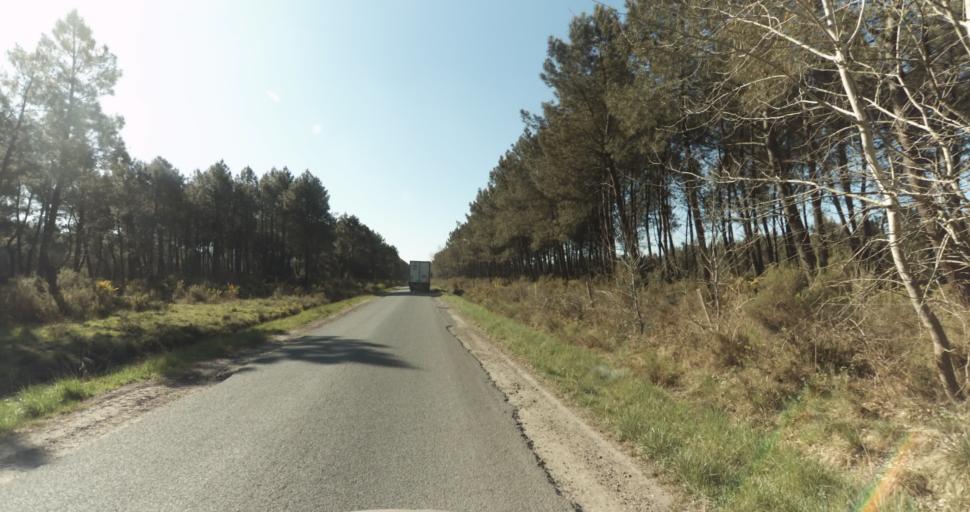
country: FR
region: Aquitaine
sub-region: Departement de la Gironde
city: Marcheprime
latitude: 44.7603
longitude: -0.8524
